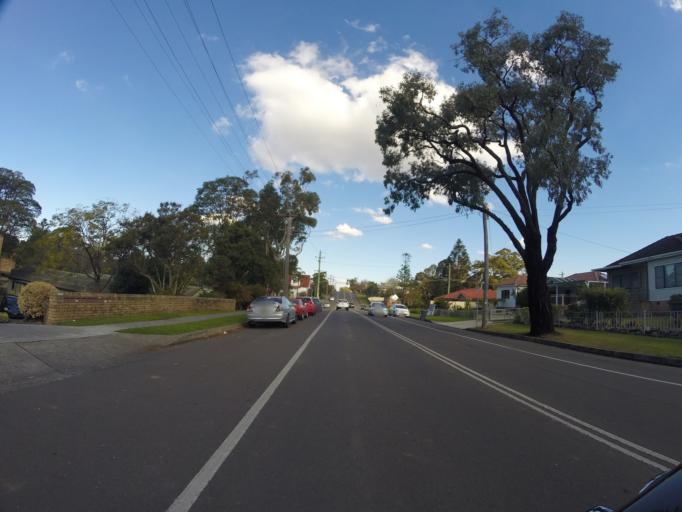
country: AU
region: New South Wales
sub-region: Wollongong
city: Keiraville
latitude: -34.4118
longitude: 150.8709
